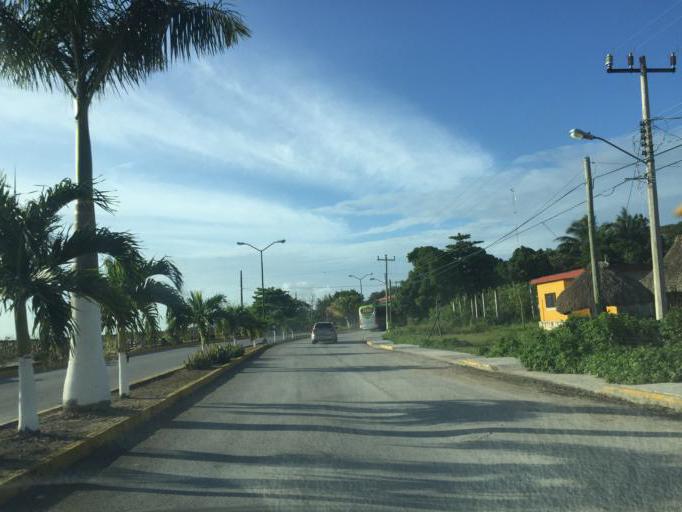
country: MX
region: Quintana Roo
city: Coba
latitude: 20.4930
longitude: -87.7355
